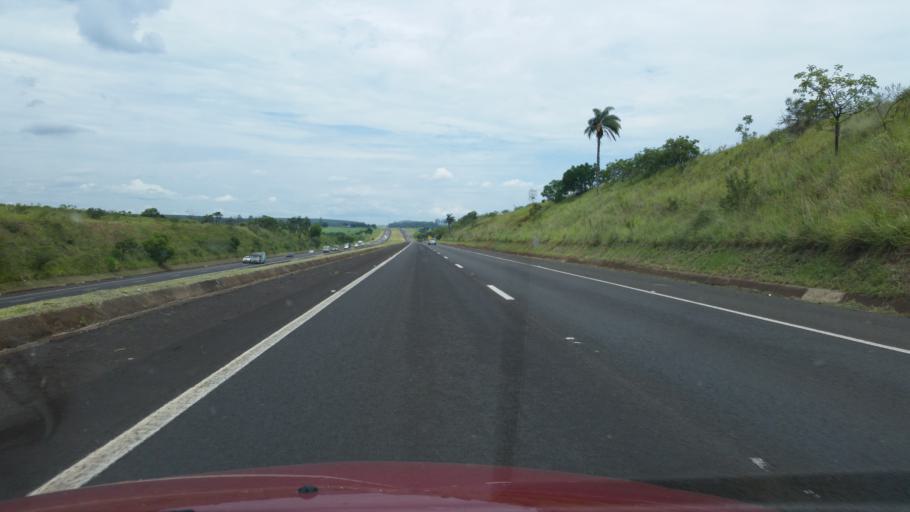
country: BR
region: Sao Paulo
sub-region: Avare
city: Avare
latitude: -22.9806
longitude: -48.7771
